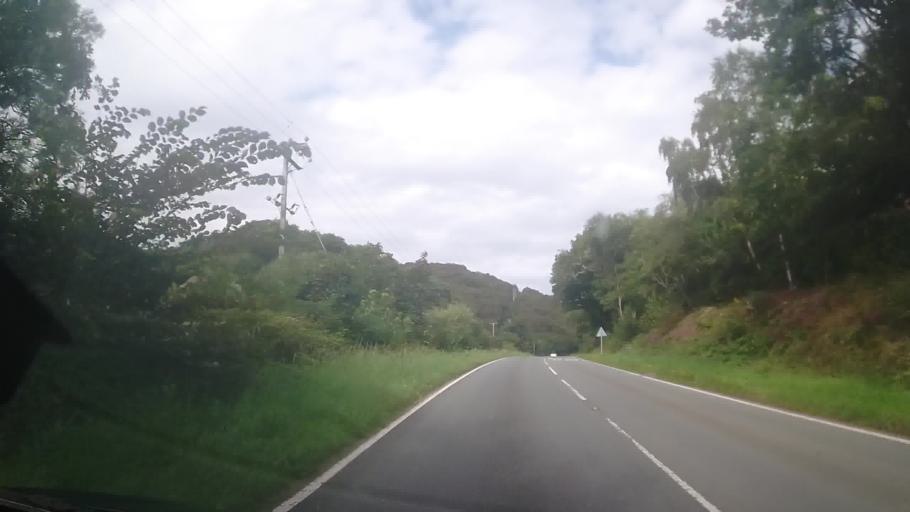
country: GB
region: Wales
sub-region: Gwynedd
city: Barmouth
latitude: 52.7170
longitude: -4.0024
